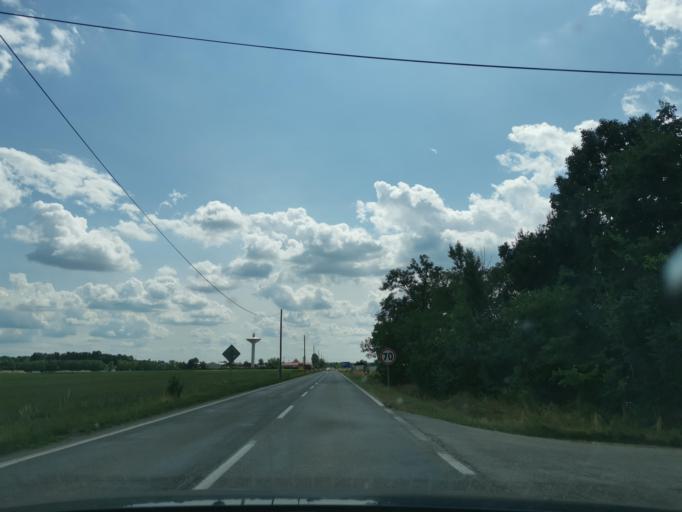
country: AT
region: Lower Austria
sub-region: Politischer Bezirk Mistelbach
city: Rabensburg
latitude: 48.5983
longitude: 16.9948
